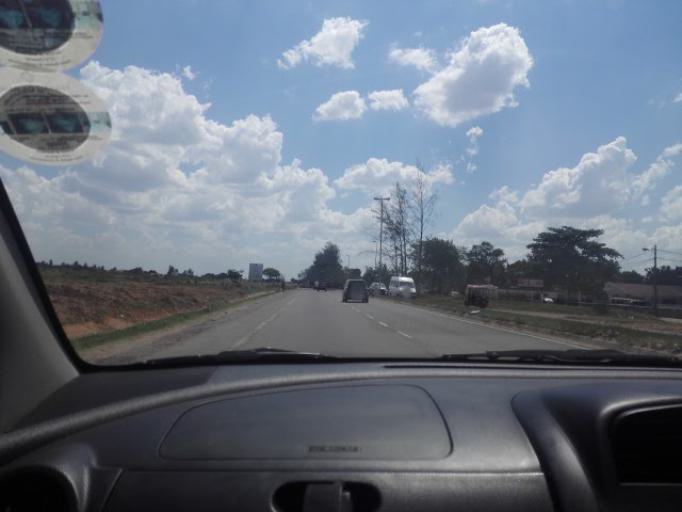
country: MZ
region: Maputo
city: Matola
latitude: -25.9545
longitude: 32.4588
